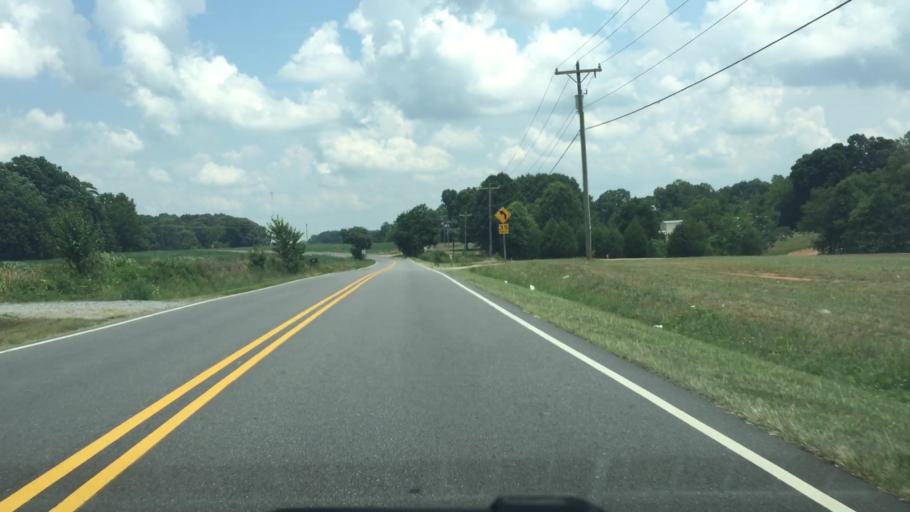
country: US
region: North Carolina
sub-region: Iredell County
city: Troutman
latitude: 35.7186
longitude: -80.8780
